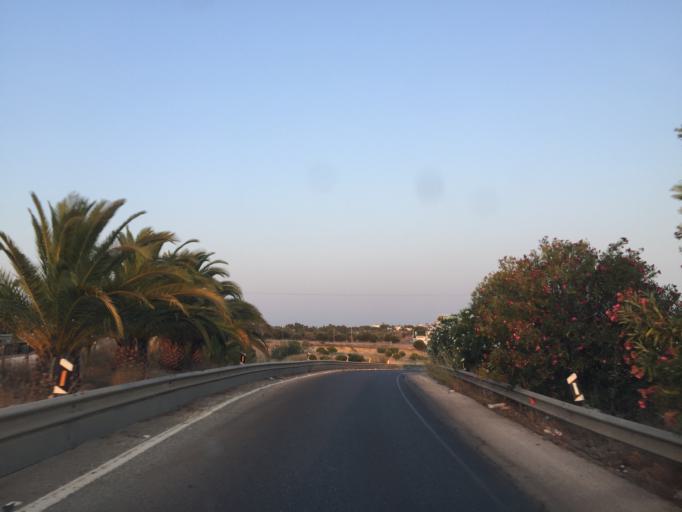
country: PT
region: Faro
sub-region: Loule
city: Almancil
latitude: 37.0837
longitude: -8.0147
